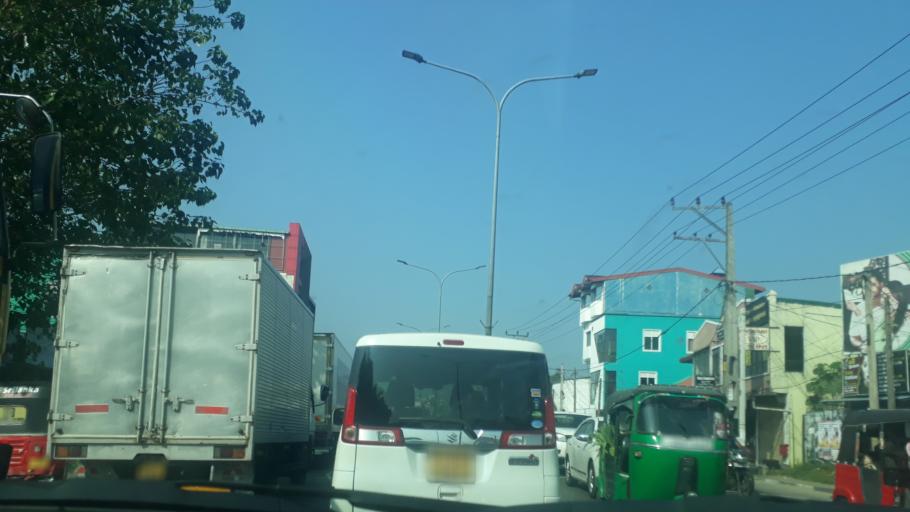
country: LK
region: Western
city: Kelaniya
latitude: 6.9698
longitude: 79.9135
